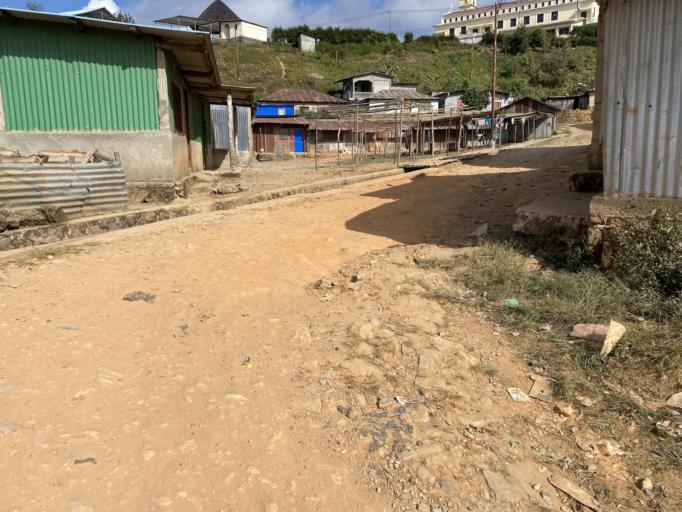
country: TL
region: Ermera
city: Gleno
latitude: -8.8363
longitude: 125.4313
